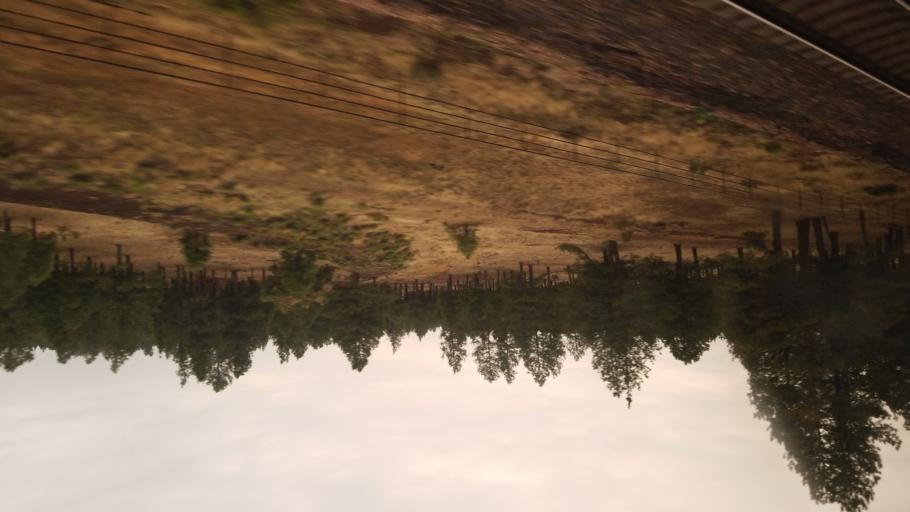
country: US
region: Arizona
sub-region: Coconino County
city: Parks
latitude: 35.2355
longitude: -112.0024
